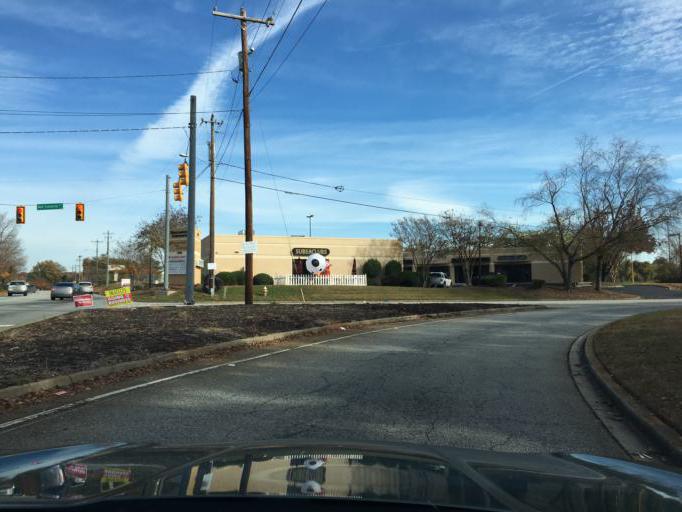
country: US
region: South Carolina
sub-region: Greenville County
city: Wade Hampton
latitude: 34.8474
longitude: -82.3331
